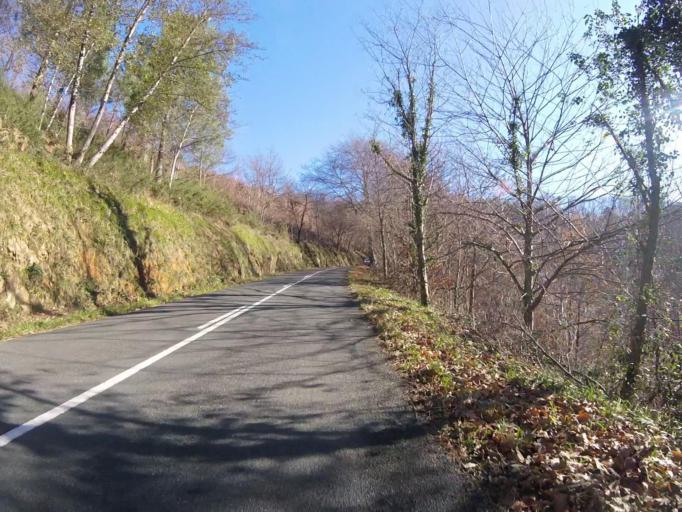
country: ES
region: Basque Country
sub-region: Provincia de Guipuzcoa
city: Irun
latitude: 43.3182
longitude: -1.7643
